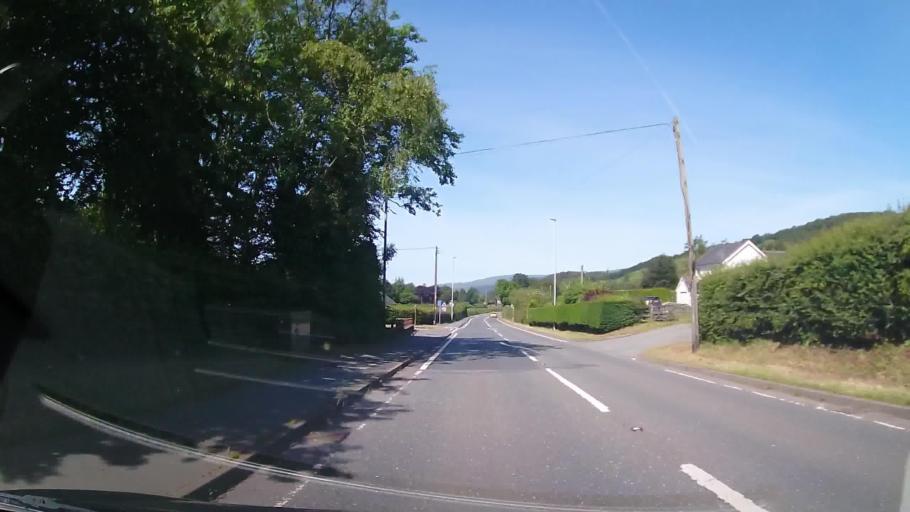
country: GB
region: Wales
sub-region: Sir Powys
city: Machynlleth
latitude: 52.5923
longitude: -3.8105
